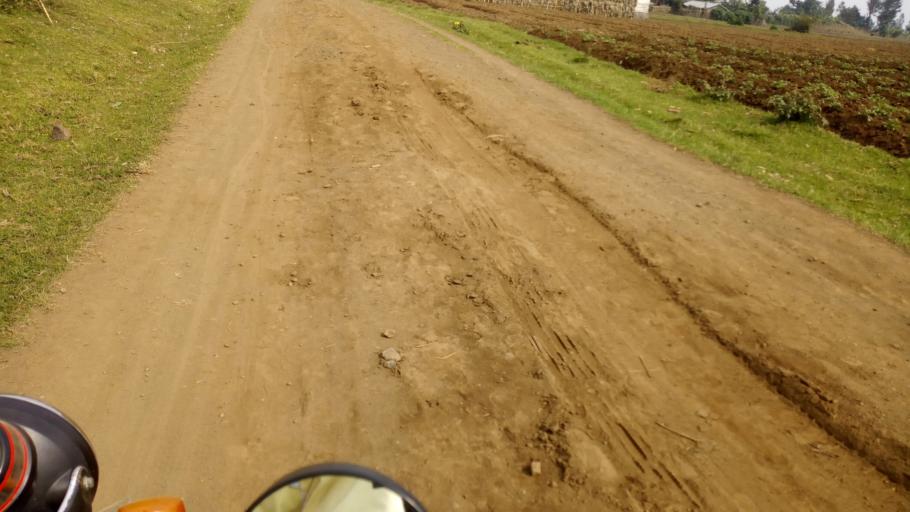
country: UG
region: Western Region
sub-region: Kisoro District
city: Kisoro
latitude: -1.3321
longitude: 29.6119
